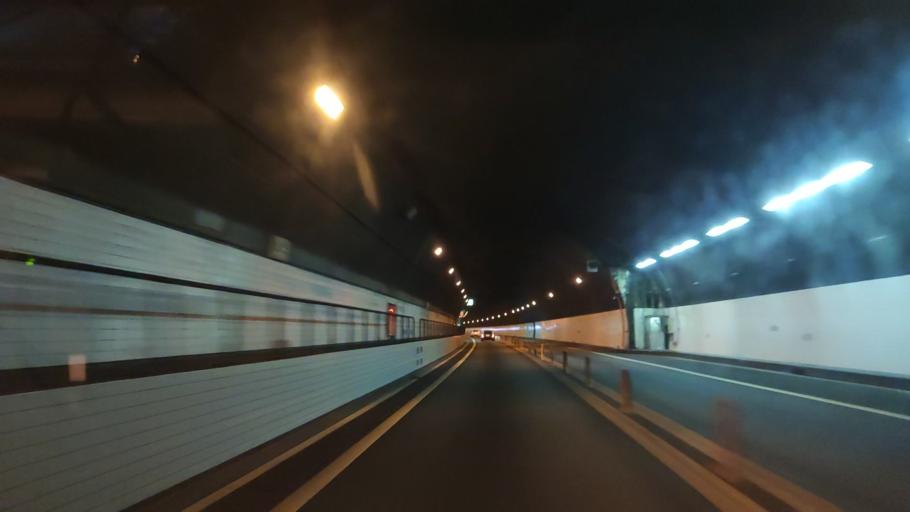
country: JP
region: Tokushima
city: Ikedacho
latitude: 34.0239
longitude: 133.7737
